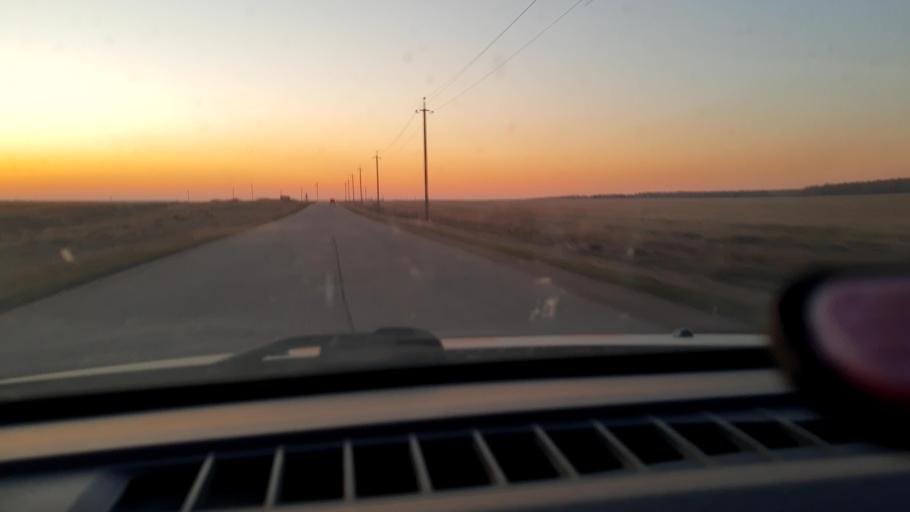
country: RU
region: Bashkortostan
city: Asanovo
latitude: 54.8050
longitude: 55.4889
